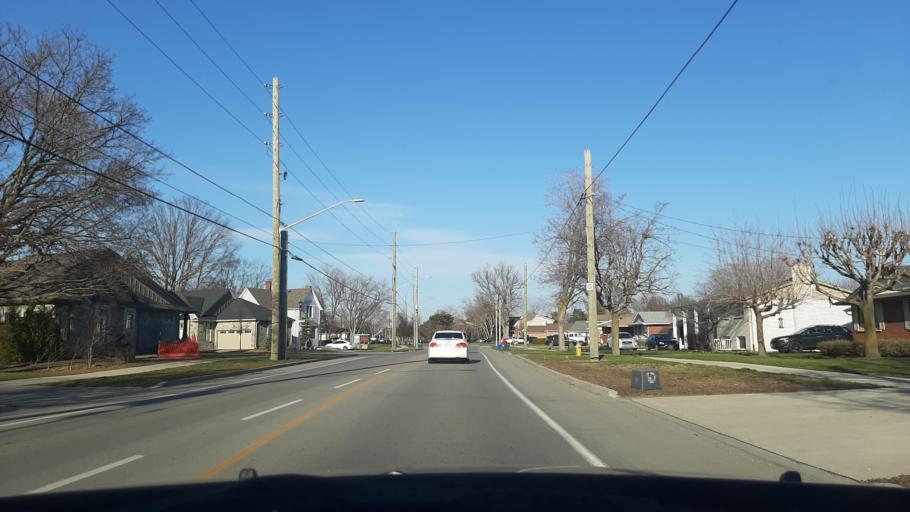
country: CA
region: Ontario
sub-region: Regional Municipality of Niagara
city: St. Catharines
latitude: 43.2012
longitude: -79.2494
